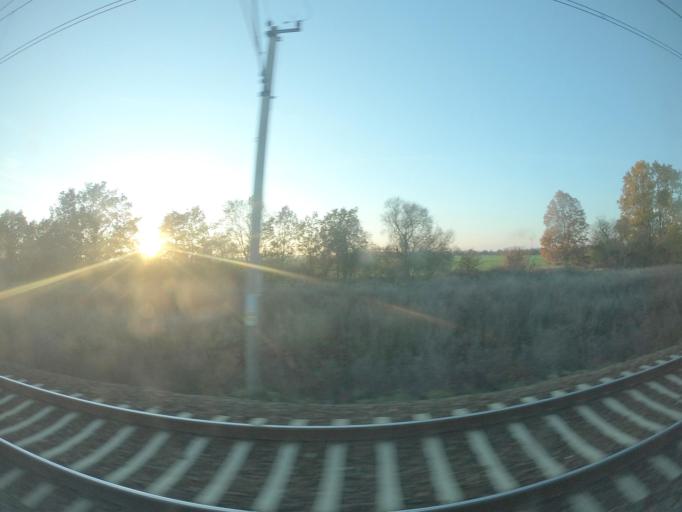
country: PL
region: Lubusz
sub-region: Powiat slubicki
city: Gorzyca
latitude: 52.5291
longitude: 14.6506
